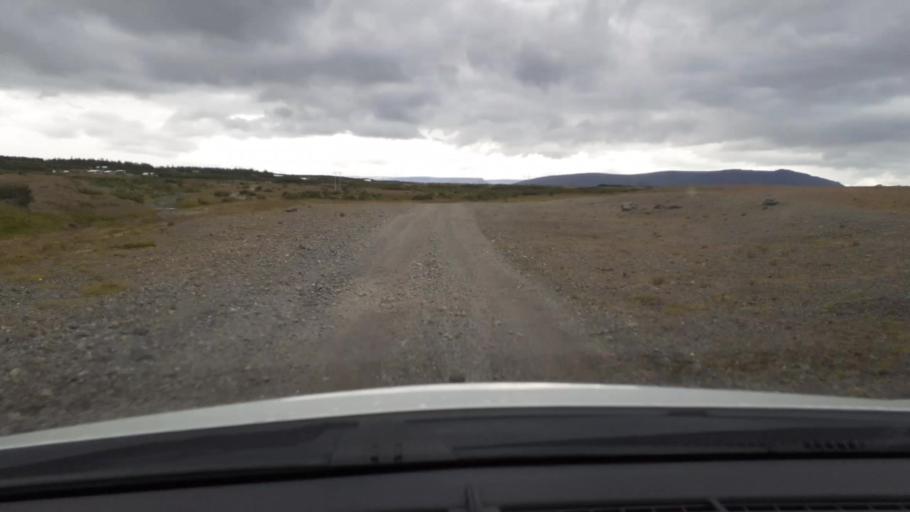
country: IS
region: West
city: Borgarnes
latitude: 64.4643
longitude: -21.9621
